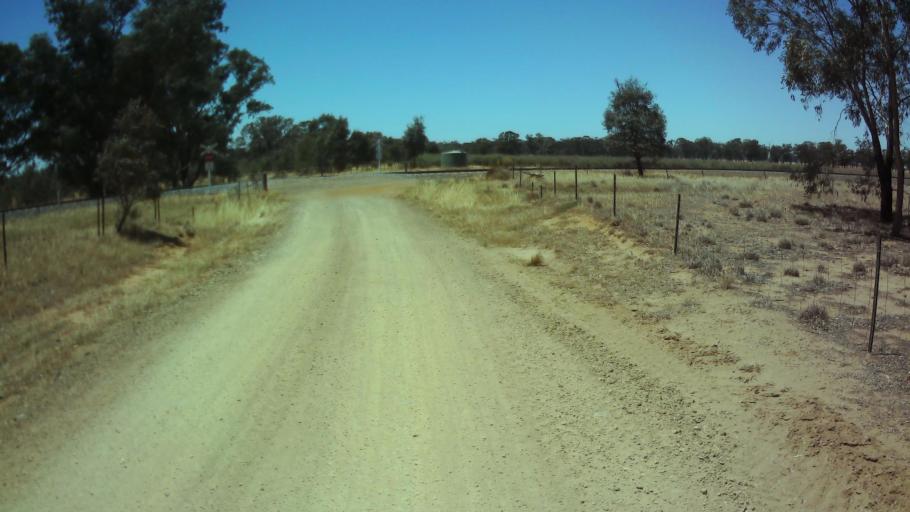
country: AU
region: New South Wales
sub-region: Weddin
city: Grenfell
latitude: -34.0478
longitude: 147.8206
